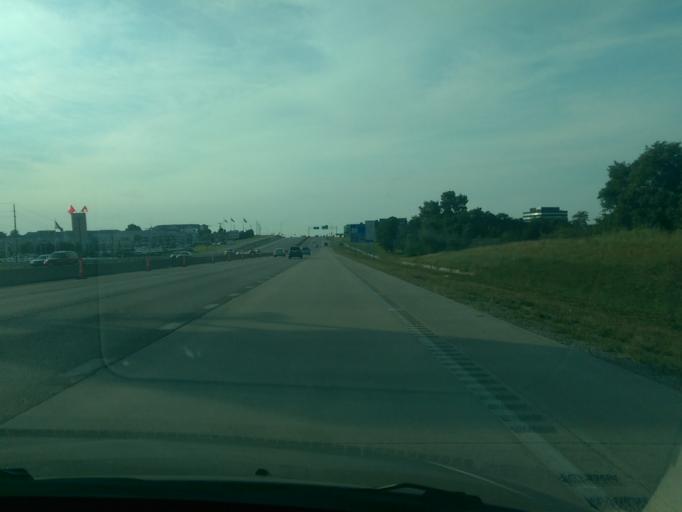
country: US
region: Missouri
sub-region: Platte County
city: Weatherby Lake
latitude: 39.2651
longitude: -94.6631
